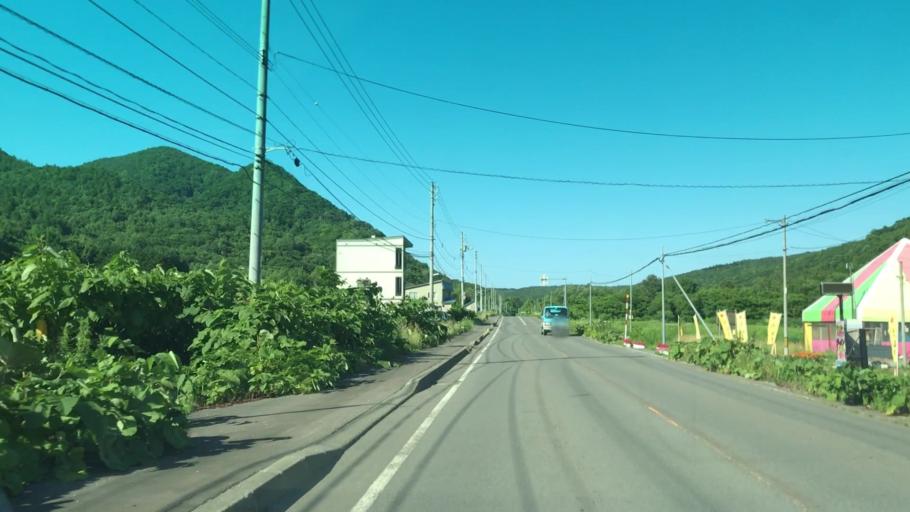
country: JP
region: Hokkaido
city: Yoichi
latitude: 43.0541
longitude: 140.8611
